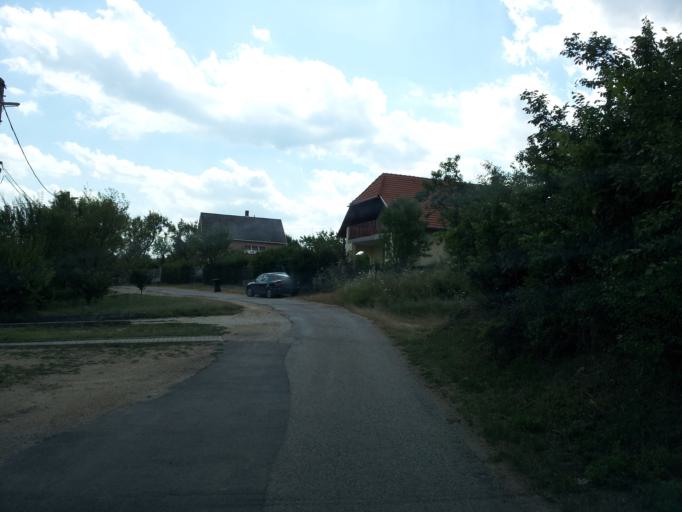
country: HU
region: Veszprem
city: Balatonalmadi
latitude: 47.0527
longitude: 18.0137
